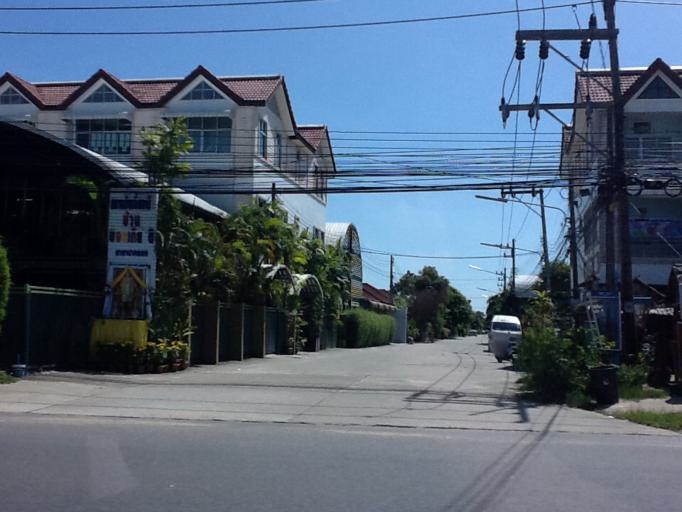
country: TH
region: Phuket
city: Thalang
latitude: 7.9883
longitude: 98.3715
